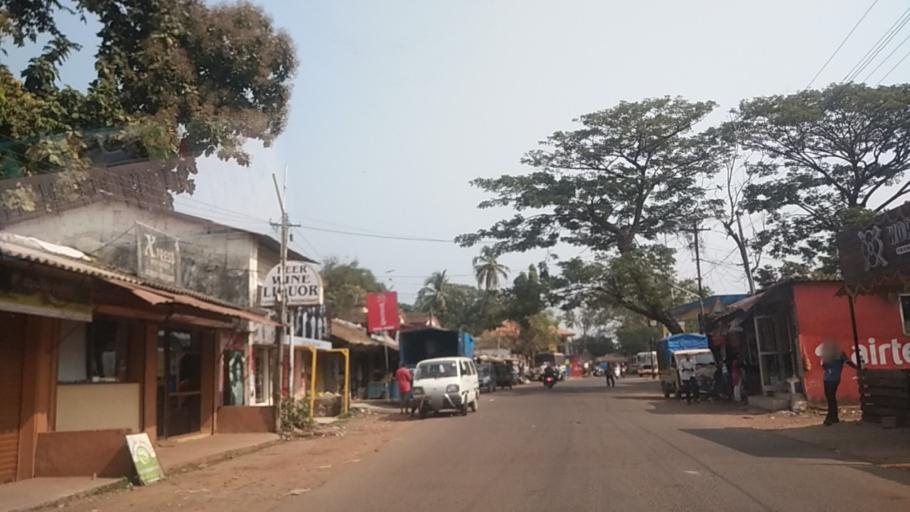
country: IN
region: Goa
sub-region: North Goa
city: Panaji
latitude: 15.5065
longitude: 73.8251
